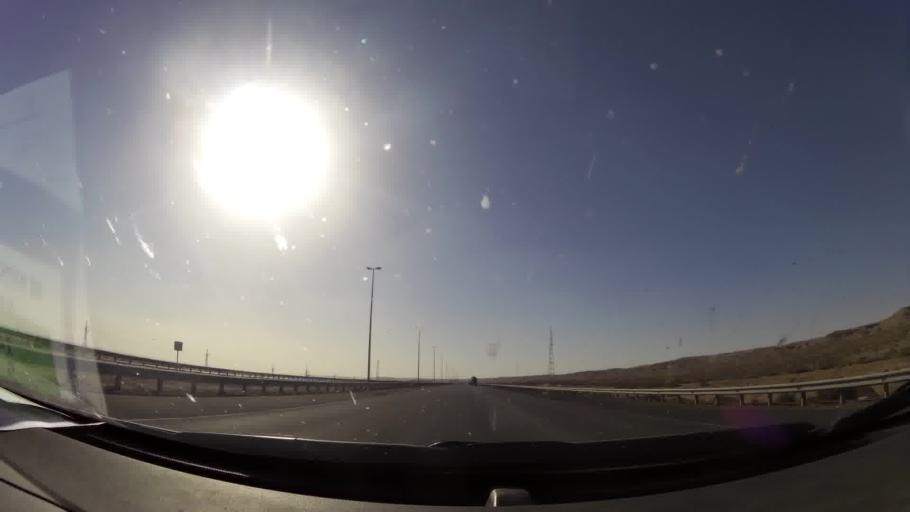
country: KW
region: Al Asimah
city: Kuwait City
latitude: 29.5367
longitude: 47.8419
